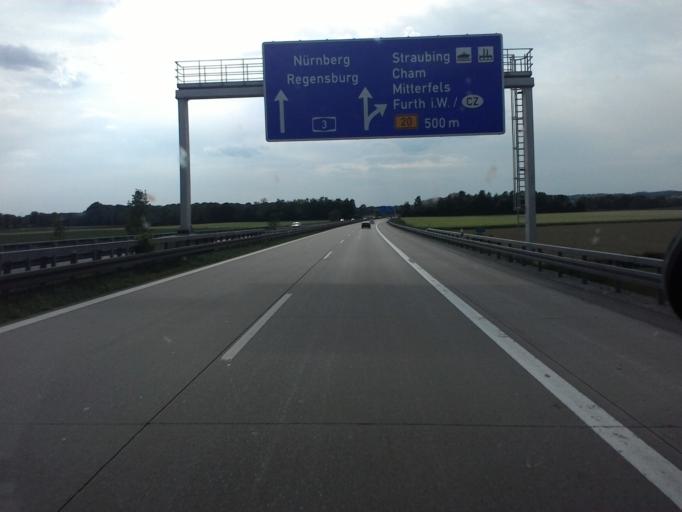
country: DE
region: Bavaria
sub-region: Lower Bavaria
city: Steinach
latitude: 48.9401
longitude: 12.6351
